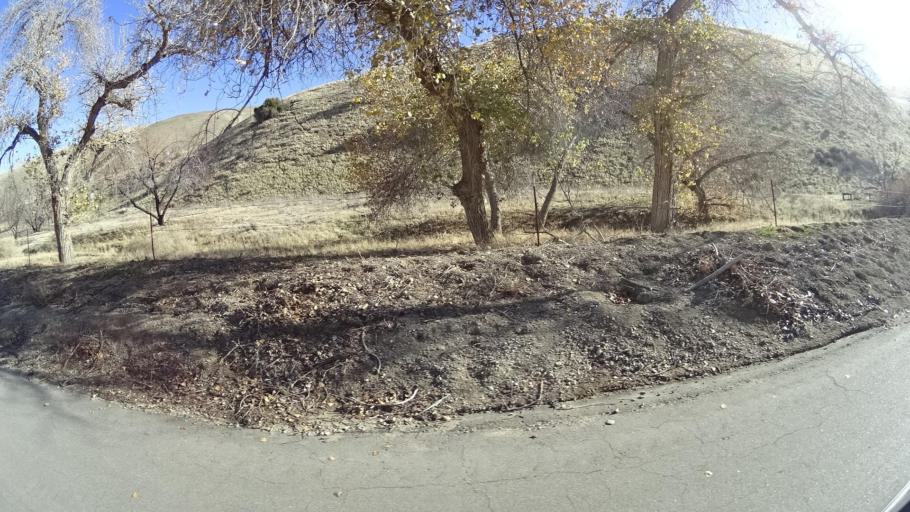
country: US
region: California
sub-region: Kern County
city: Maricopa
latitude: 34.9748
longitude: -119.4096
